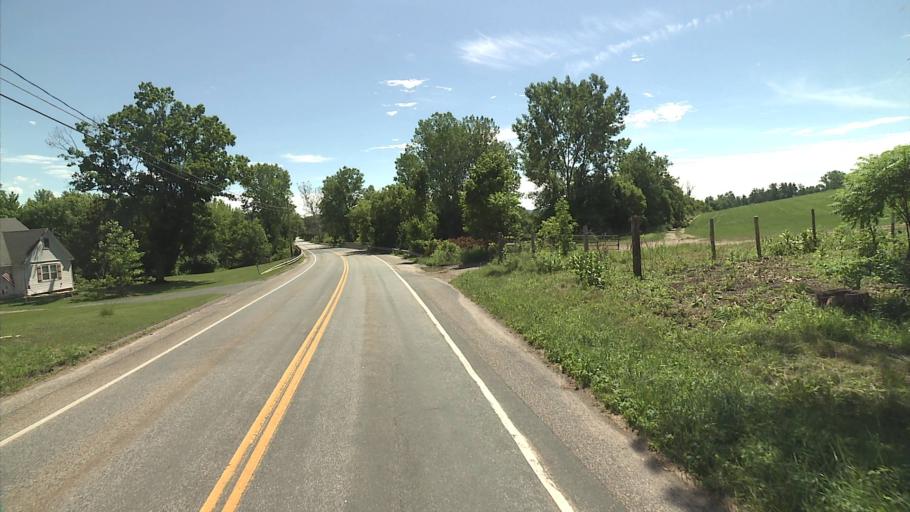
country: US
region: Connecticut
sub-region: Litchfield County
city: Canaan
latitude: 42.0464
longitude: -73.3124
